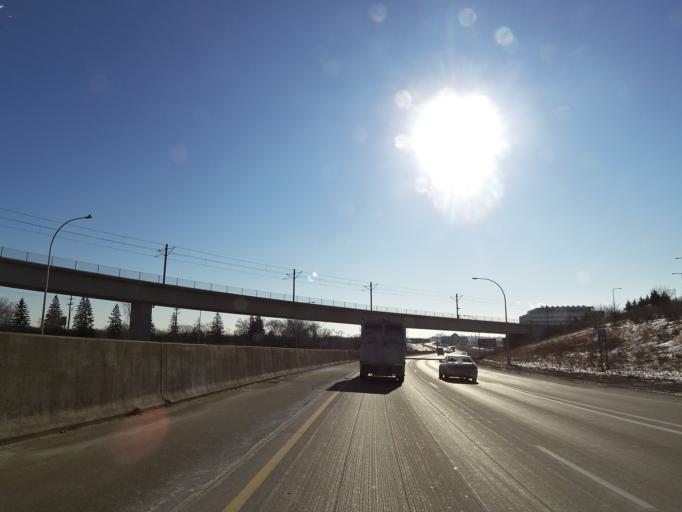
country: US
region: Minnesota
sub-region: Dakota County
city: Mendota Heights
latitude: 44.8982
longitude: -93.1991
